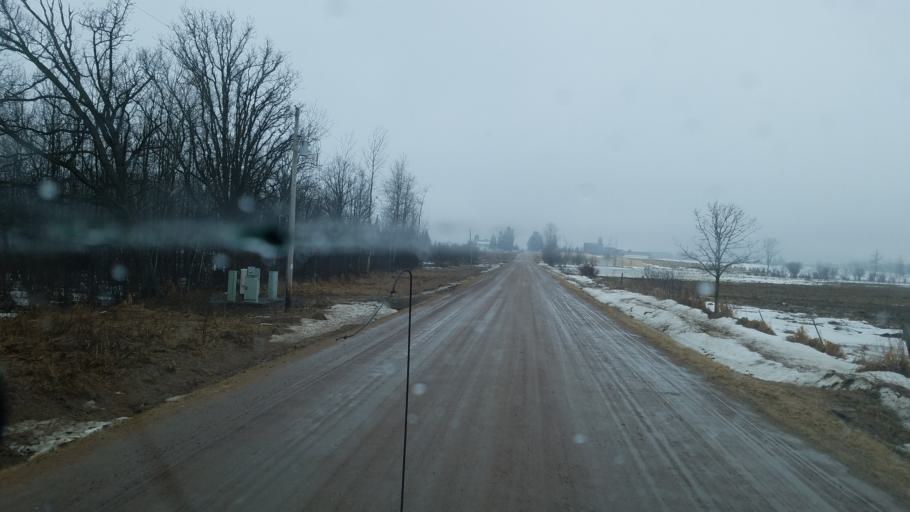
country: US
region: Wisconsin
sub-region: Clark County
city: Loyal
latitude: 44.6541
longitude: -90.3978
